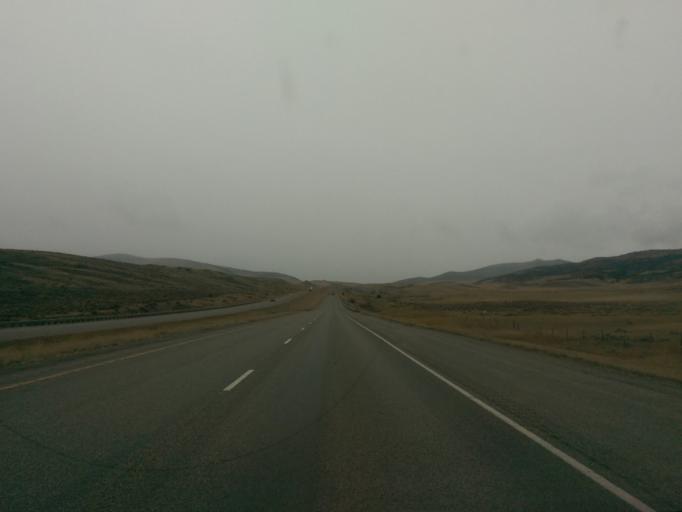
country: US
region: Montana
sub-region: Gallatin County
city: Three Forks
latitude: 45.9084
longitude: -111.7932
